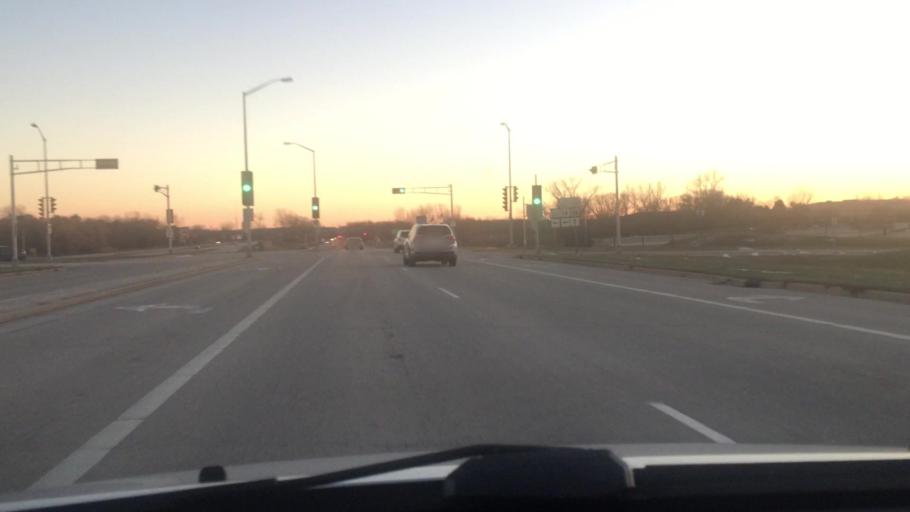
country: US
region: Wisconsin
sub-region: Waukesha County
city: Pewaukee
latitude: 43.0721
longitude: -88.2525
